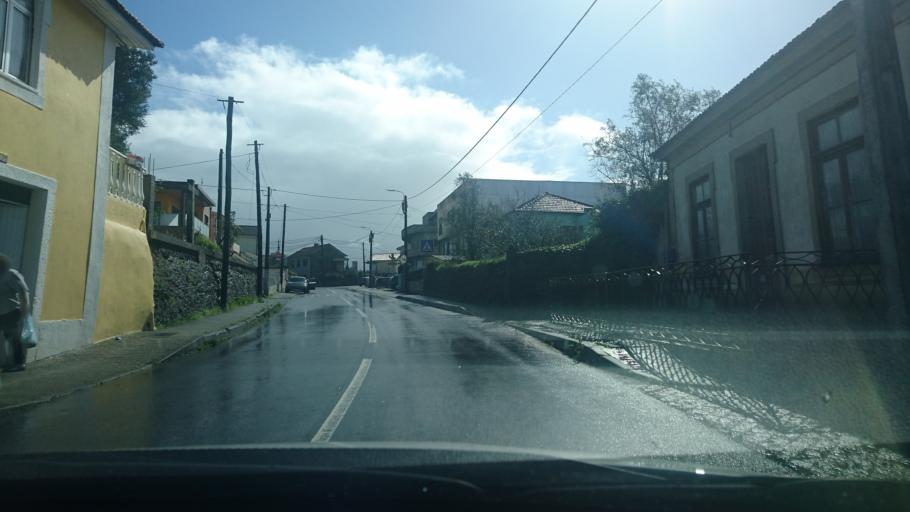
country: PT
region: Porto
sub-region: Paredes
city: Recarei
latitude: 41.1516
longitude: -8.4080
